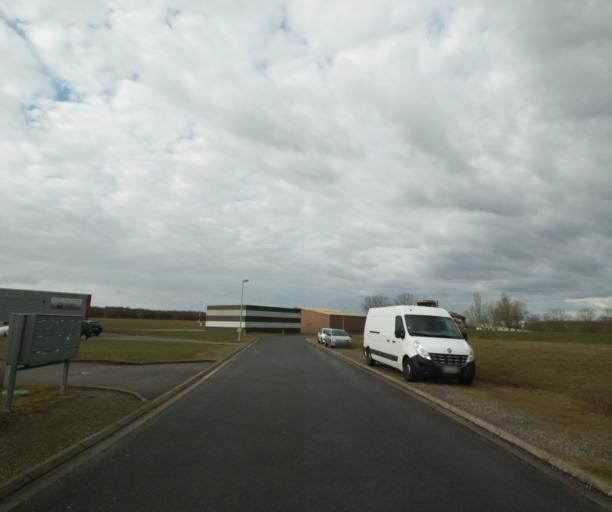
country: FR
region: Auvergne
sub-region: Departement de l'Allier
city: Toulon-sur-Allier
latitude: 46.5375
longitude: 3.4241
